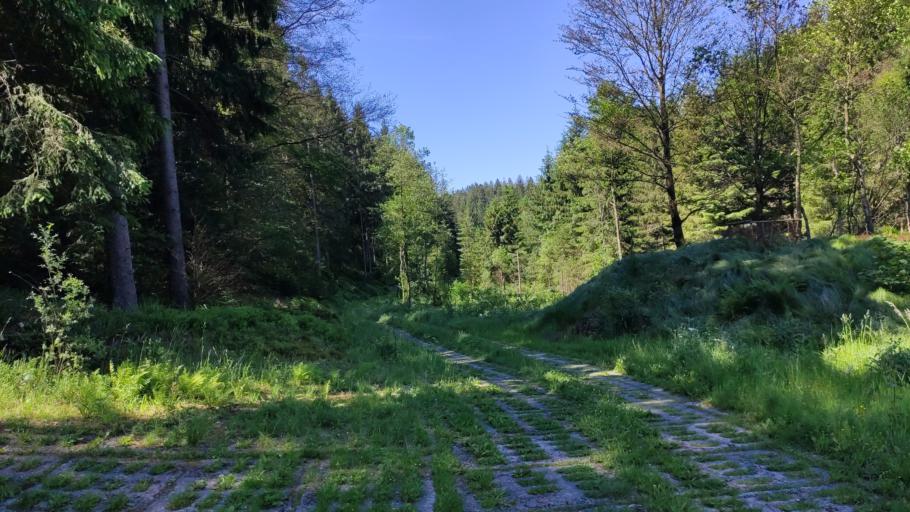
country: DE
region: Bavaria
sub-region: Upper Franconia
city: Tschirn
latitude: 50.4332
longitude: 11.4550
